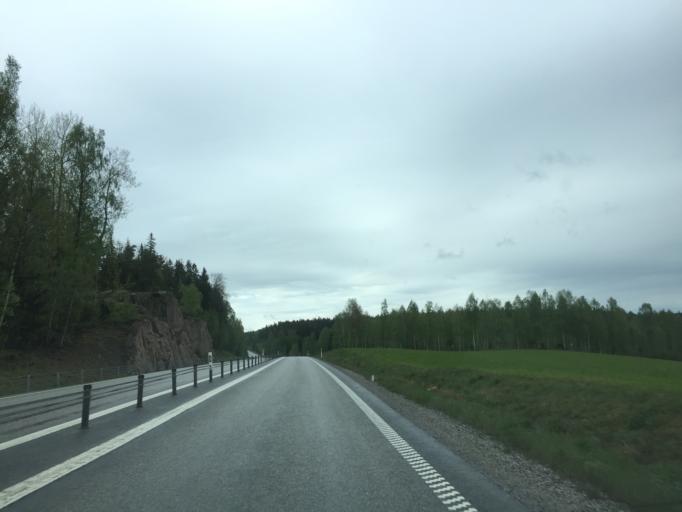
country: SE
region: OErebro
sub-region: Nora Kommun
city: Nora
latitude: 59.4909
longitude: 15.1457
